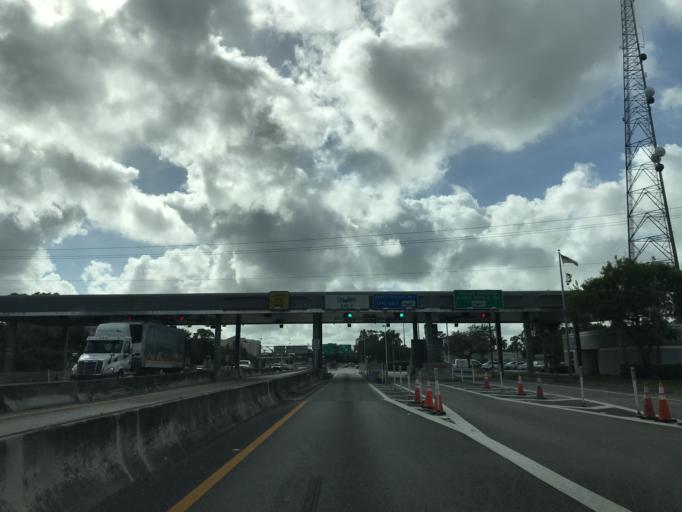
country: US
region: Florida
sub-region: Palm Beach County
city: Boca Del Mar
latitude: 26.3713
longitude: -80.1692
